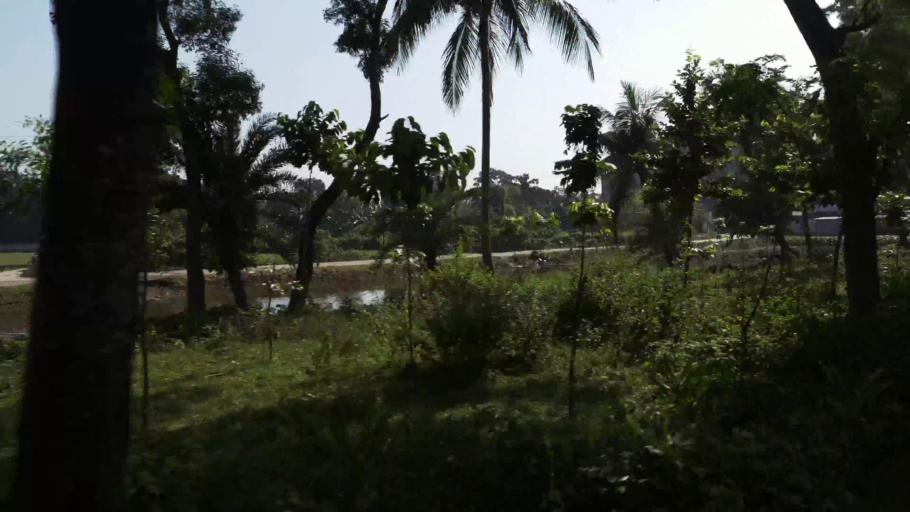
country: BD
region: Dhaka
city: Mymensingh
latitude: 24.6011
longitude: 90.4937
